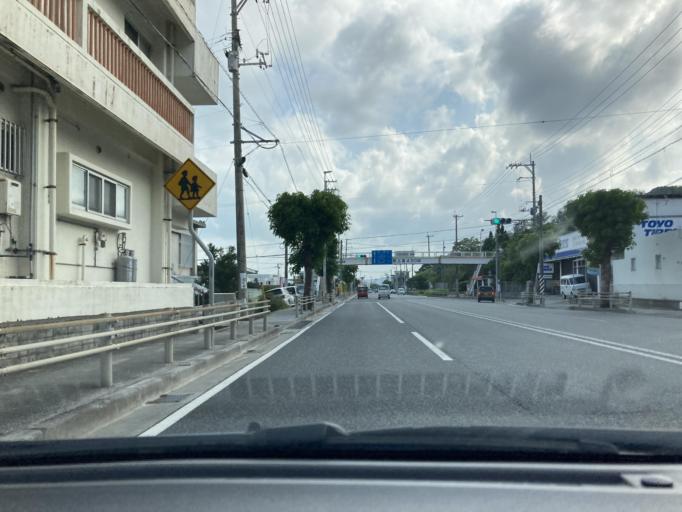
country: JP
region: Okinawa
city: Ginowan
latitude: 26.2493
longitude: 127.7824
